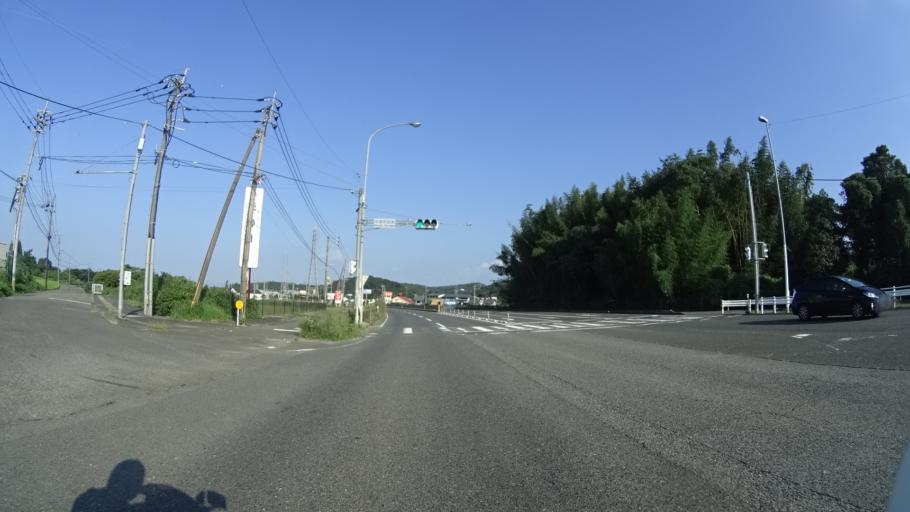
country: JP
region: Fukuoka
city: Nakatsu
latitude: 33.5526
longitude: 131.2096
